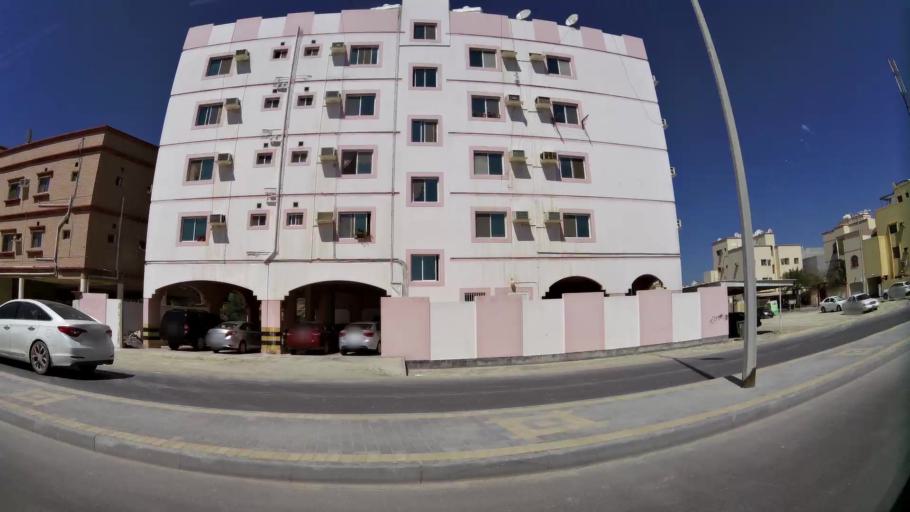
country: BH
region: Muharraq
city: Al Hadd
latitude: 26.2759
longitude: 50.6440
